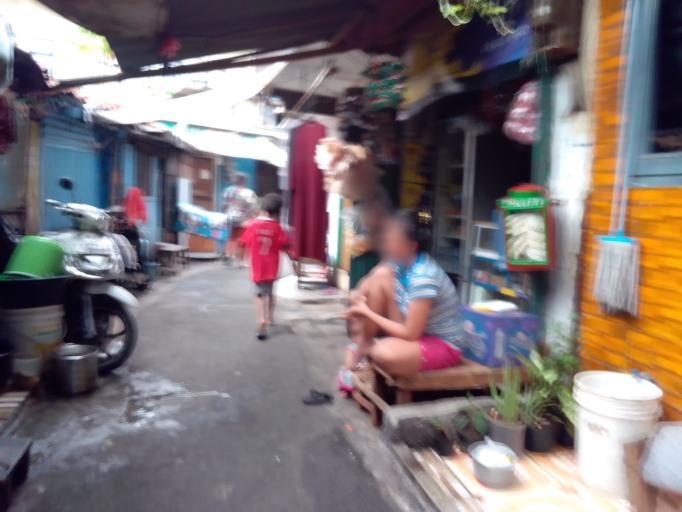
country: ID
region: Jakarta Raya
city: Jakarta
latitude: -6.1551
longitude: 106.8121
